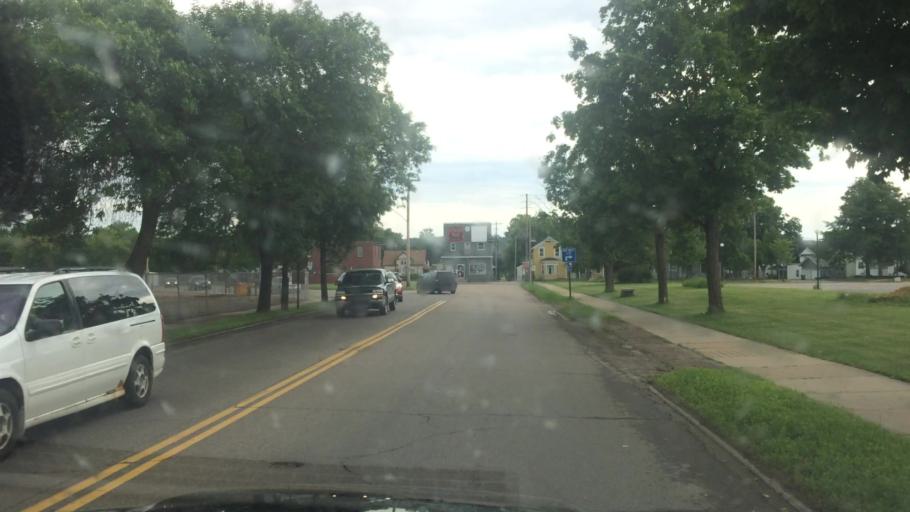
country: US
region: Wisconsin
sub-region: Marathon County
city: Wausau
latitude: 44.9484
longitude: -89.6367
